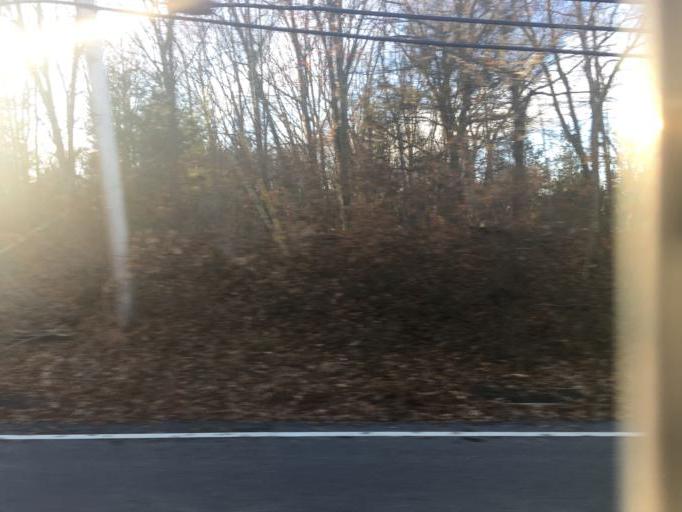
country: US
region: Rhode Island
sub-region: Kent County
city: West Warwick
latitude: 41.6936
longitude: -71.5014
